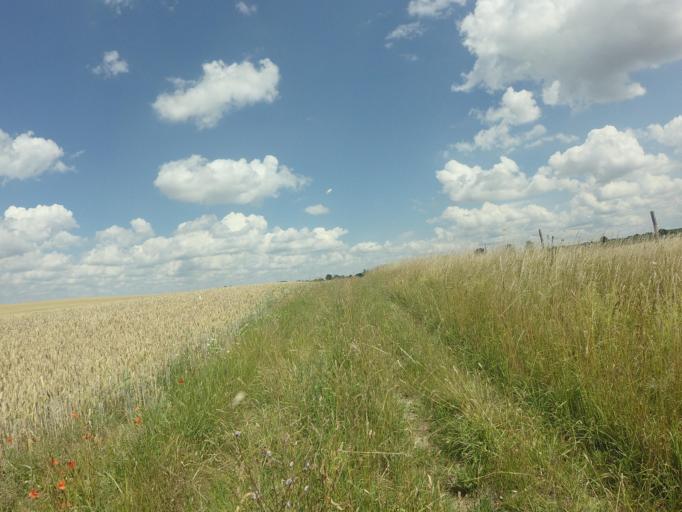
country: PL
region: West Pomeranian Voivodeship
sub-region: Powiat choszczenski
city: Recz
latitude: 53.2054
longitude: 15.4906
